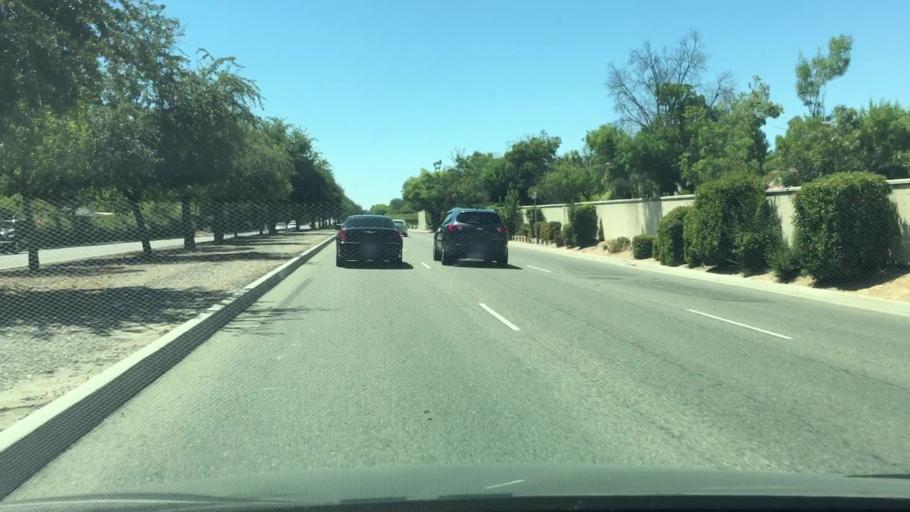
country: US
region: California
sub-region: Fresno County
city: Fresno
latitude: 36.8373
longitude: -119.8384
